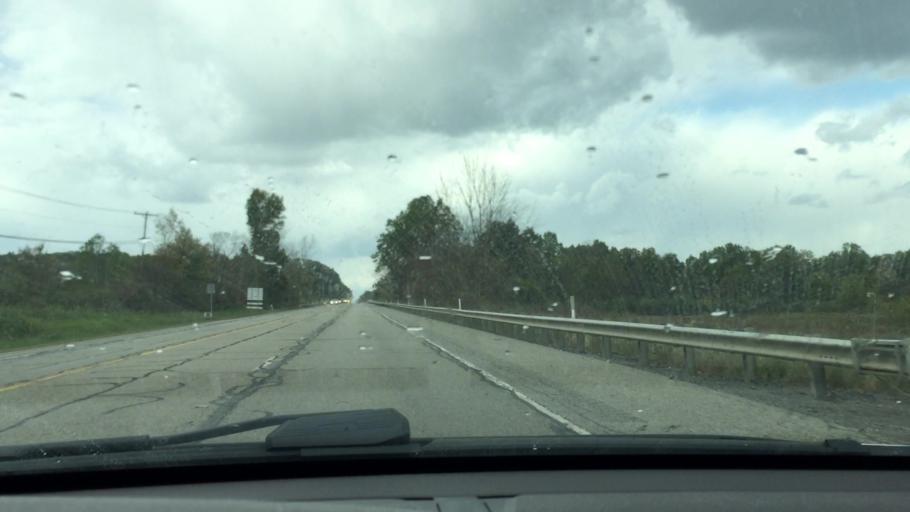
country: US
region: Pennsylvania
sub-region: Lawrence County
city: Oakwood
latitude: 41.0562
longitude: -80.4449
